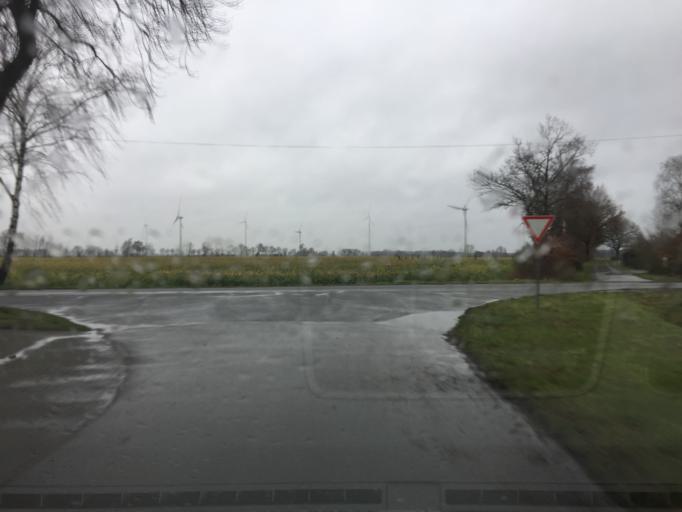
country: DE
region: Lower Saxony
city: Borstel
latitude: 52.6028
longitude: 8.9542
